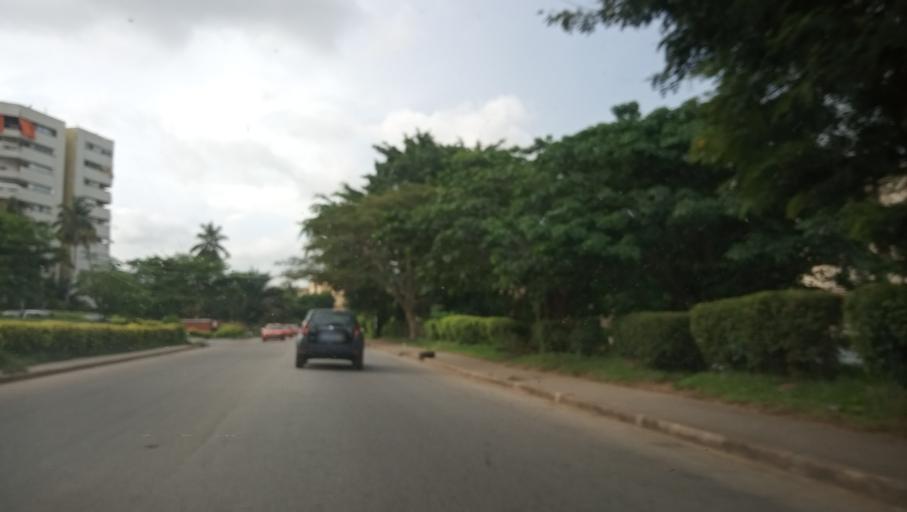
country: CI
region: Lagunes
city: Abidjan
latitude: 5.3423
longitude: -3.9761
